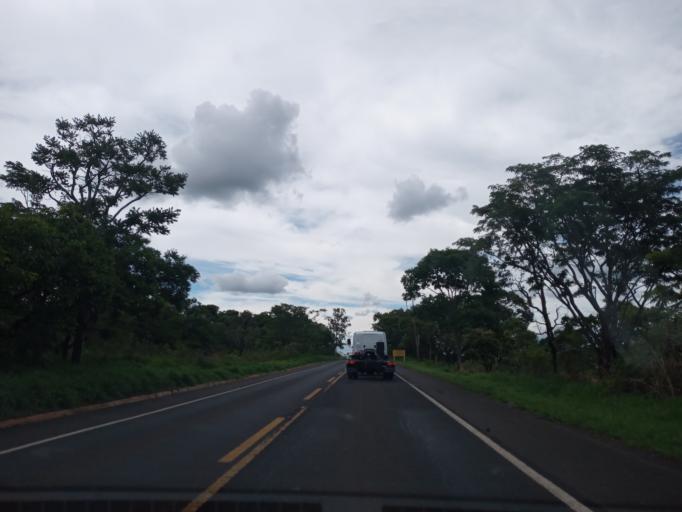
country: BR
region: Minas Gerais
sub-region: Uberlandia
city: Uberlandia
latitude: -19.1823
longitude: -47.8794
